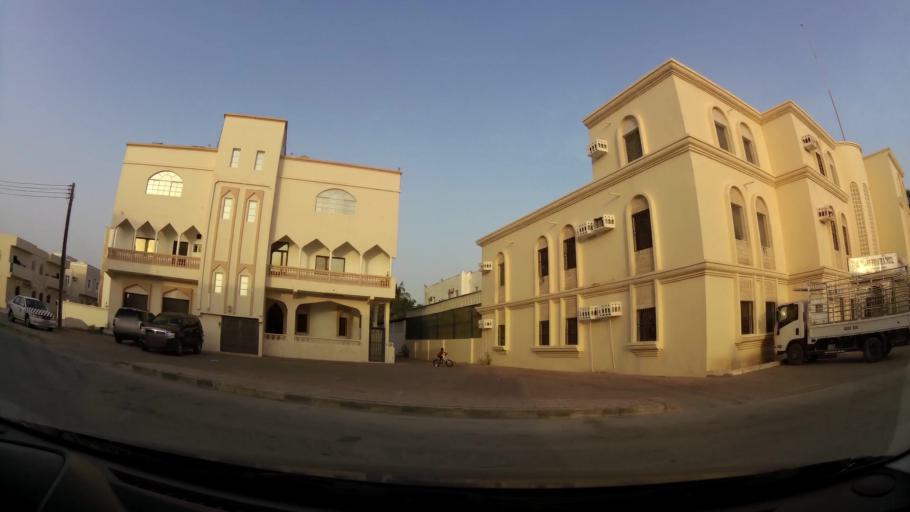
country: OM
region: Zufar
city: Salalah
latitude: 17.0180
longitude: 54.1166
